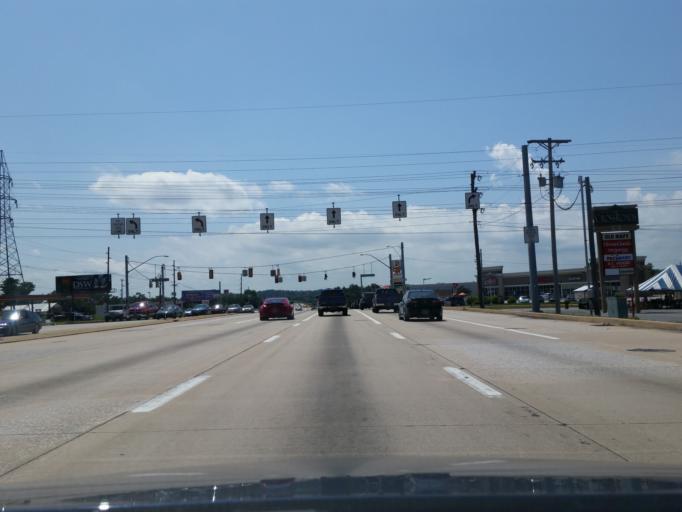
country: US
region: Pennsylvania
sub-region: York County
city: North York
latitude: 39.9823
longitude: -76.7436
